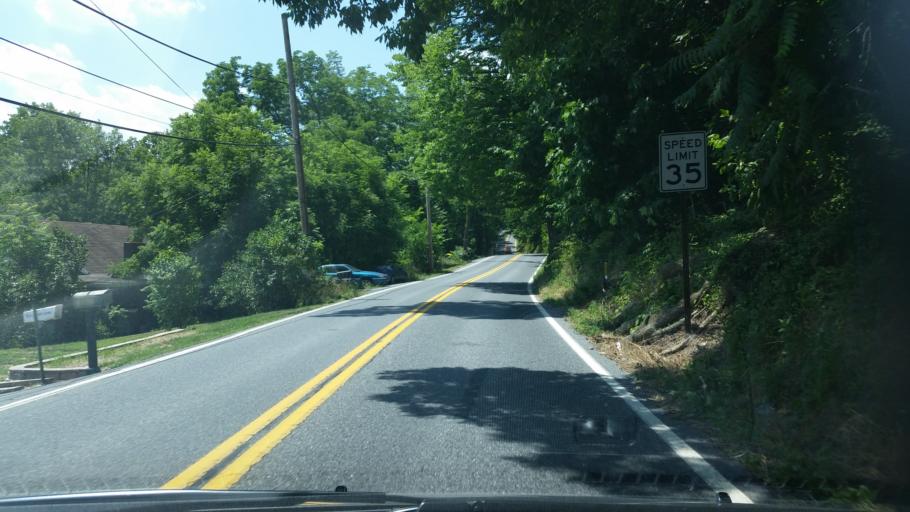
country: US
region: Pennsylvania
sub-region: Dauphin County
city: Hummelstown
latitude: 40.2912
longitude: -76.6981
